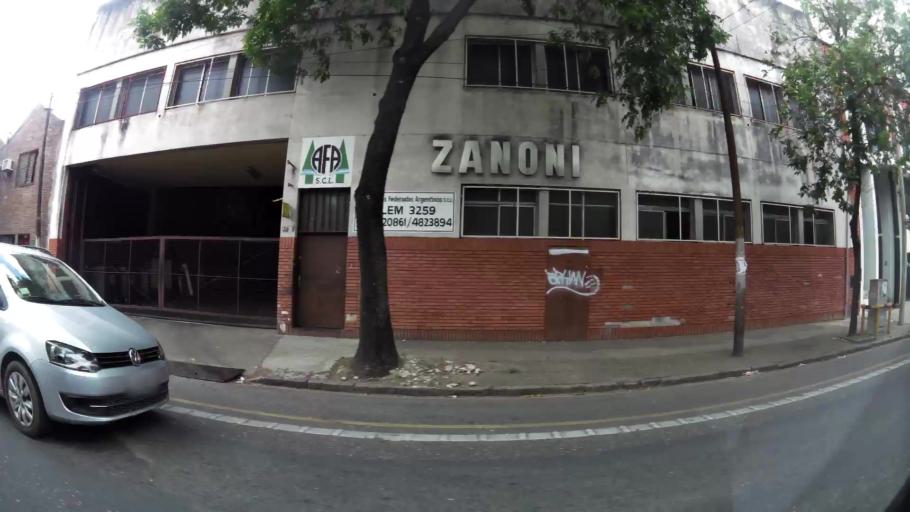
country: AR
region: Santa Fe
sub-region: Departamento de Rosario
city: Rosario
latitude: -32.9771
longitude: -60.6356
